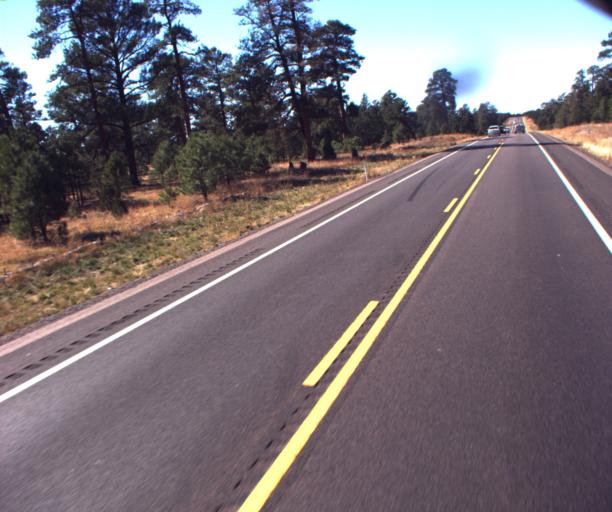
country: US
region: Arizona
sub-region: Apache County
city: Saint Michaels
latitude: 35.7003
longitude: -109.2901
